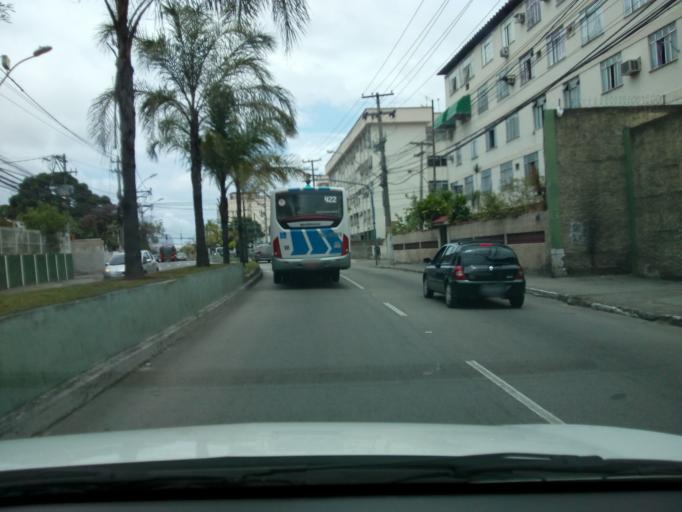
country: BR
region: Rio de Janeiro
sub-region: Niteroi
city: Niteroi
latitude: -22.8737
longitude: -43.1063
